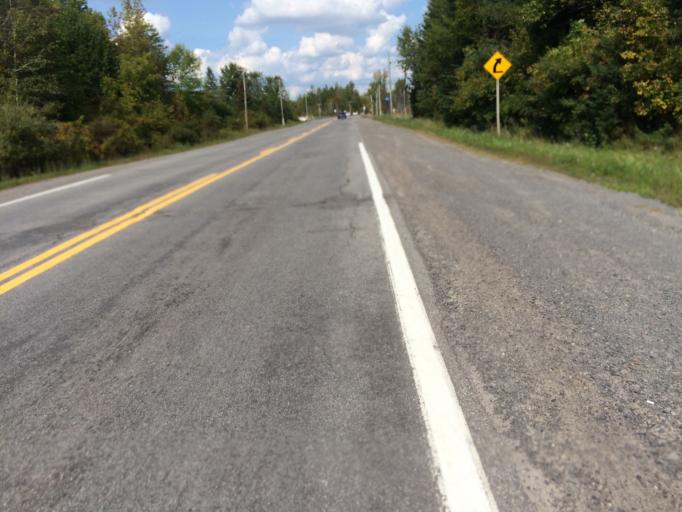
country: CA
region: Ontario
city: Bells Corners
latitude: 45.1729
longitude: -75.6400
